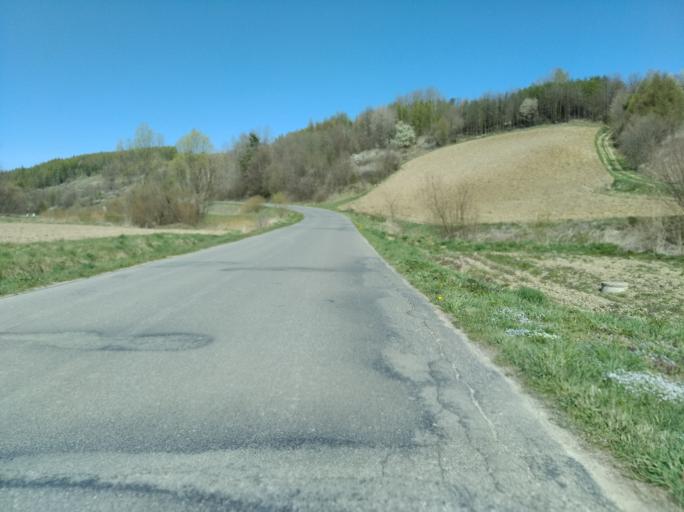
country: PL
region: Subcarpathian Voivodeship
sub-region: Powiat brzozowski
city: Dydnia
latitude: 49.7021
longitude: 22.1525
